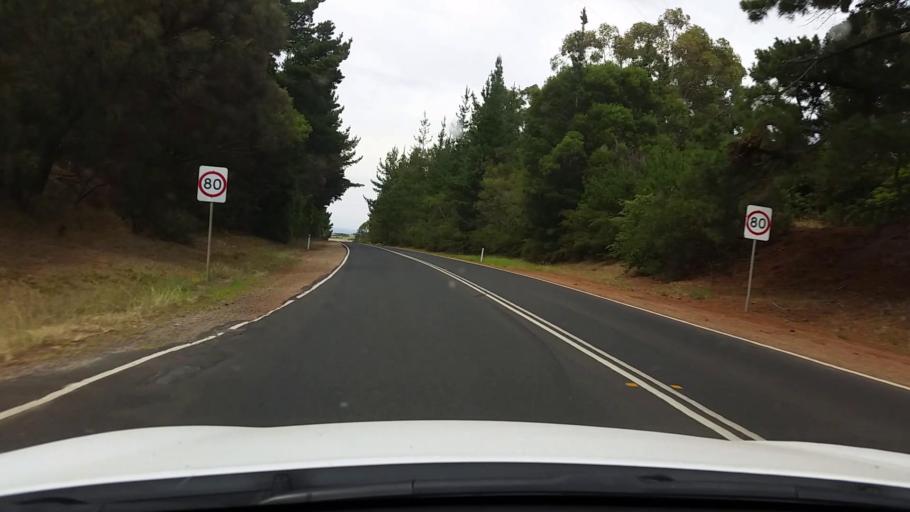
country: AU
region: Victoria
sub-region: Mornington Peninsula
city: Merricks
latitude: -38.4203
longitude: 145.0440
